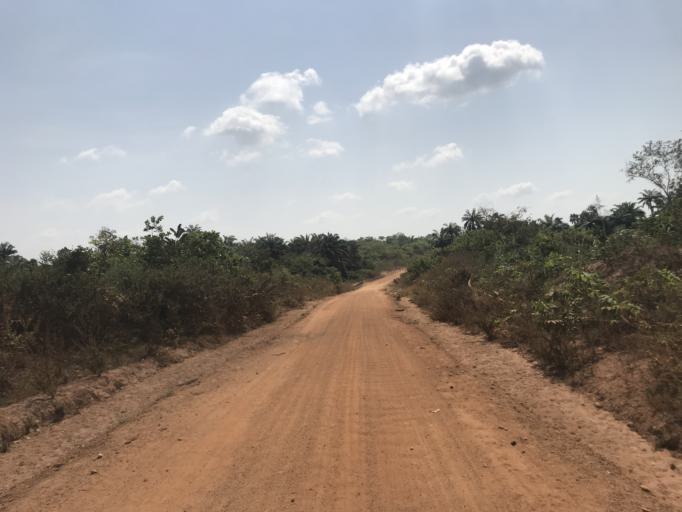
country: NG
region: Osun
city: Ifon
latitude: 7.9302
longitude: 4.4830
